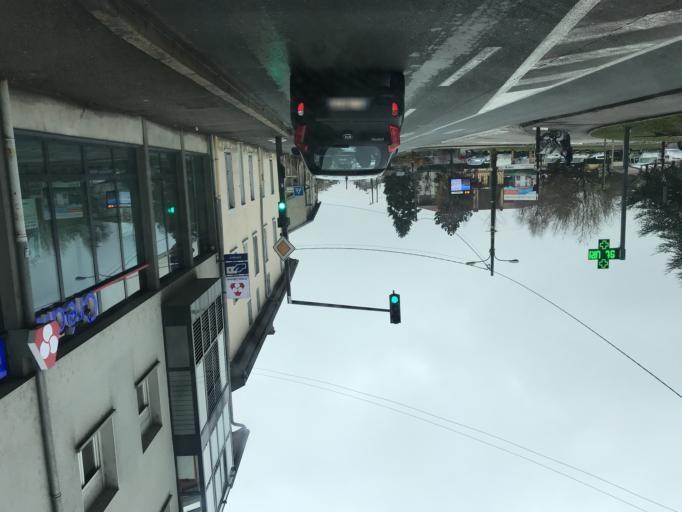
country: FR
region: Rhone-Alpes
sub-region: Departement de l'Ain
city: Villars-les-Dombes
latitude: 46.0027
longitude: 5.0314
